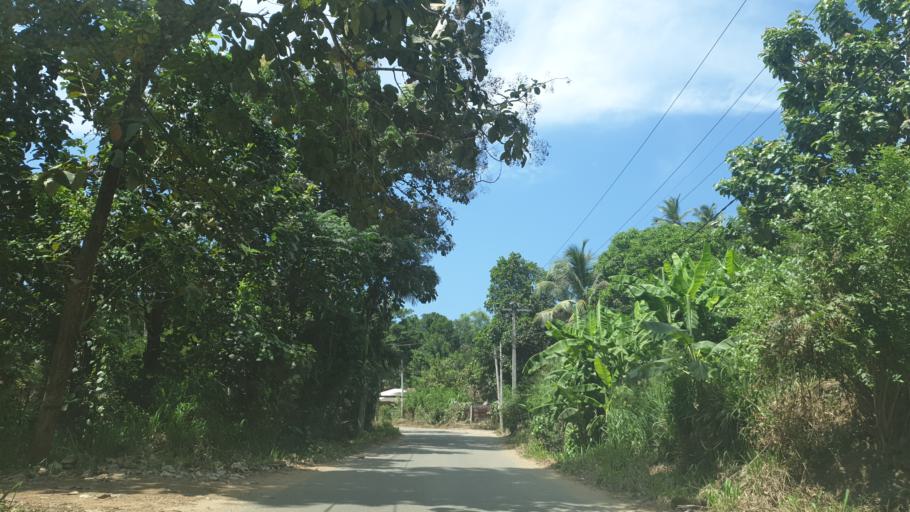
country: LK
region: Southern
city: Matara
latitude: 5.9760
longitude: 80.6612
